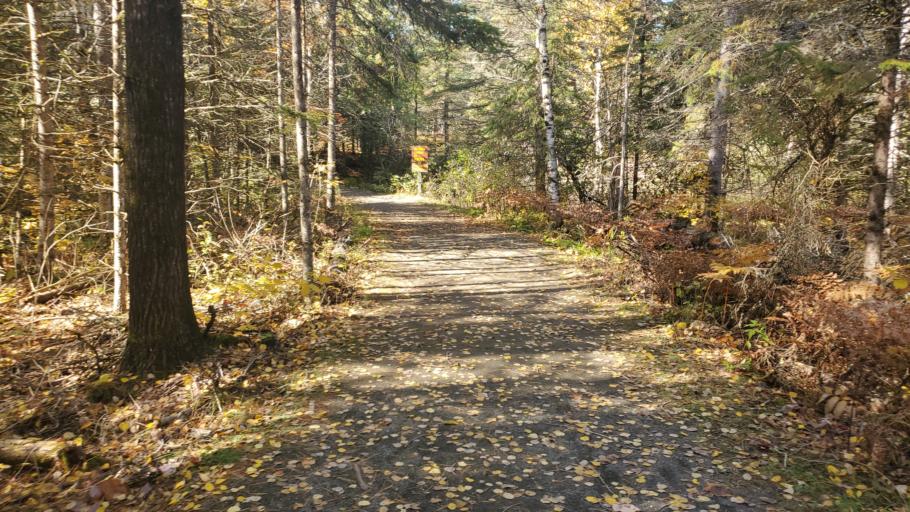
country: CA
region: Ontario
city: Peterborough
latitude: 44.6199
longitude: -78.0474
